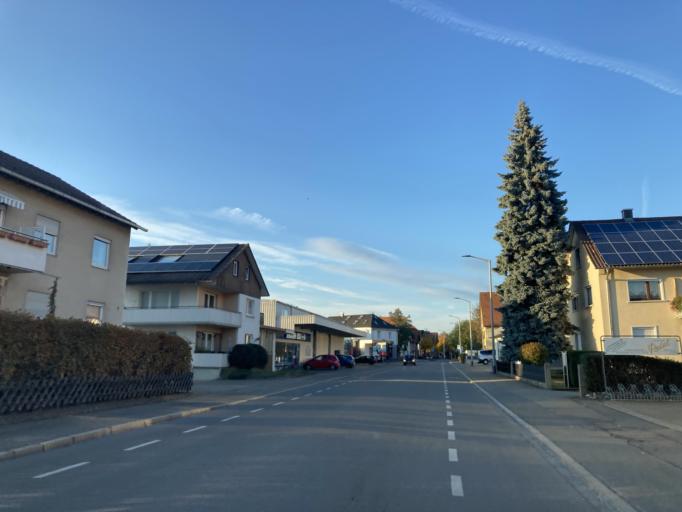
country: DE
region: Baden-Wuerttemberg
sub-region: Freiburg Region
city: Villingen-Schwenningen
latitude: 48.0496
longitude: 8.4619
